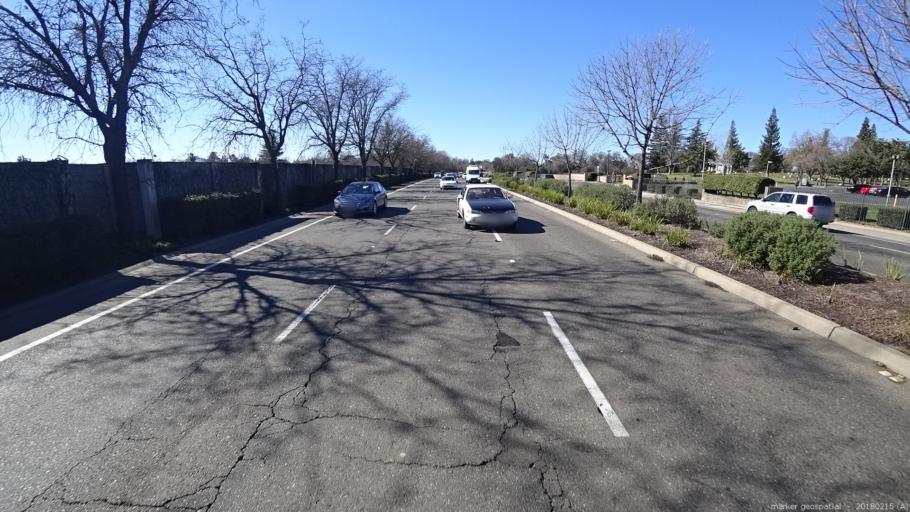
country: US
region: California
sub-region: Sacramento County
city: Foothill Farms
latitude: 38.6809
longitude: -121.3287
